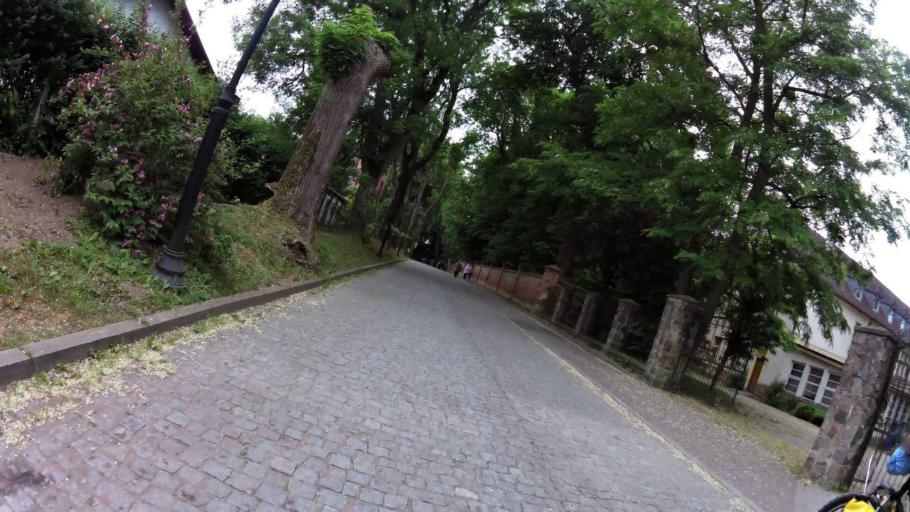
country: PL
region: West Pomeranian Voivodeship
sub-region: Powiat gryficki
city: Rewal
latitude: 54.0758
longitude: 14.9933
